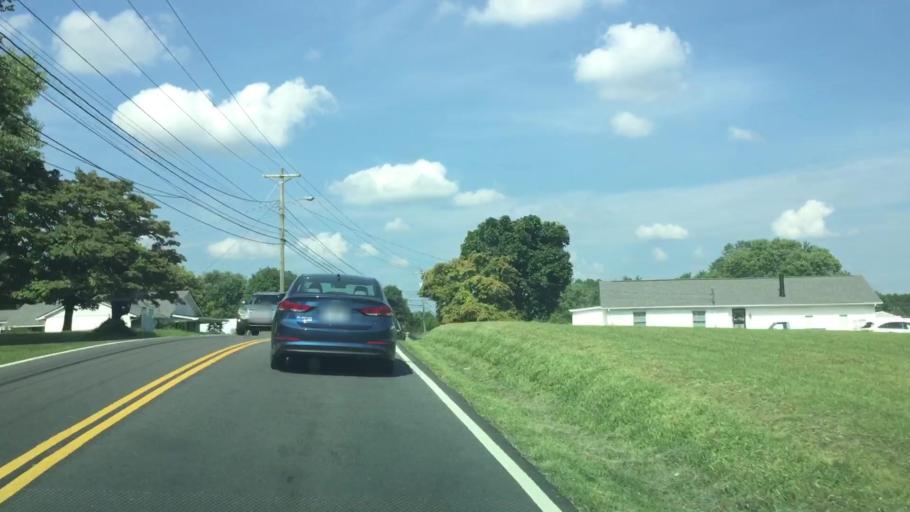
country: US
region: Tennessee
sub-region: Sullivan County
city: Fairmount
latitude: 36.6155
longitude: -82.1346
